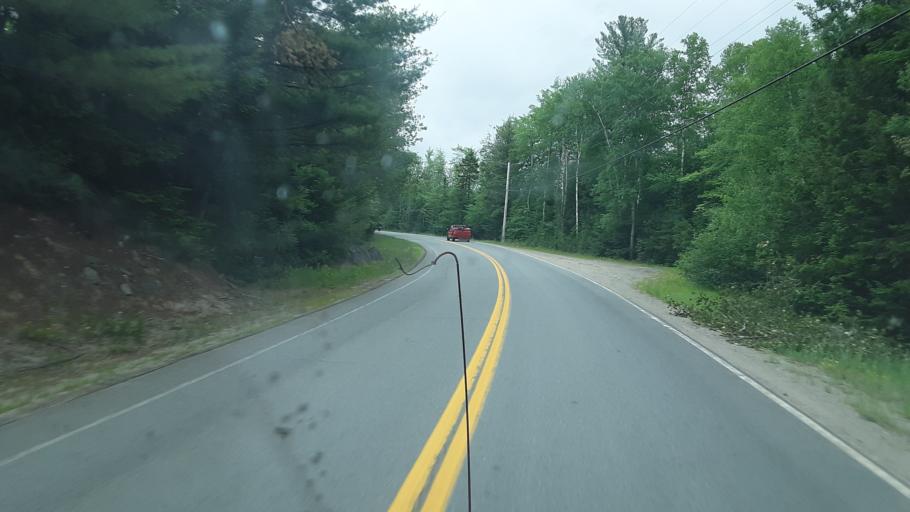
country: US
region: Maine
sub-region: Penobscot County
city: Millinocket
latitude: 45.6791
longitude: -68.7578
